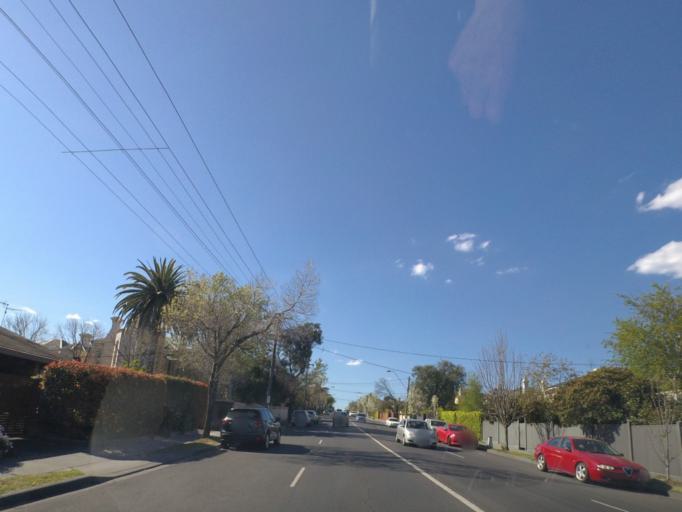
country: AU
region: Victoria
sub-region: Boroondara
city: Kew
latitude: -37.8181
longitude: 145.0270
